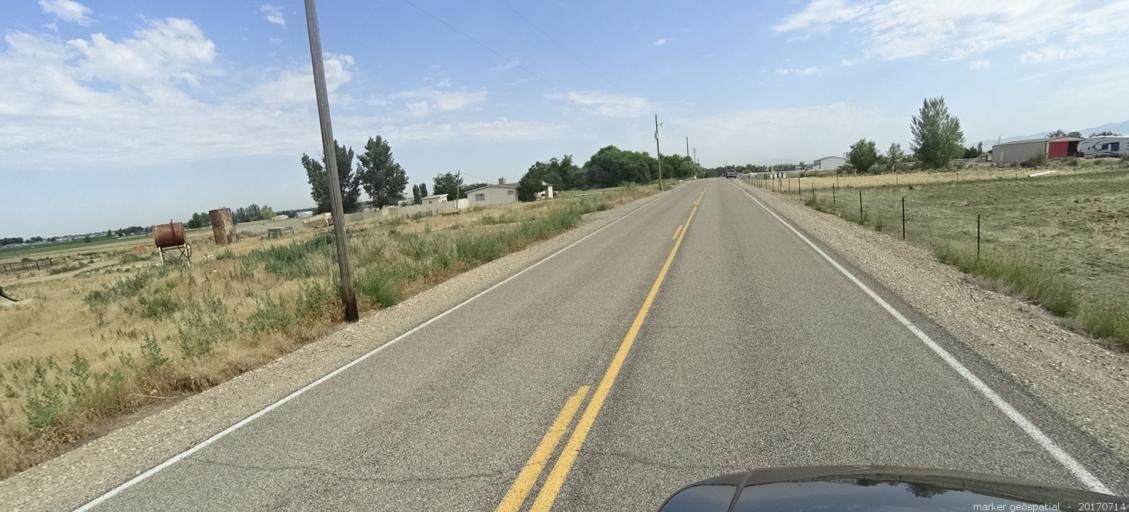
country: US
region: Idaho
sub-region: Ada County
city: Kuna
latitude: 43.4971
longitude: -116.3543
